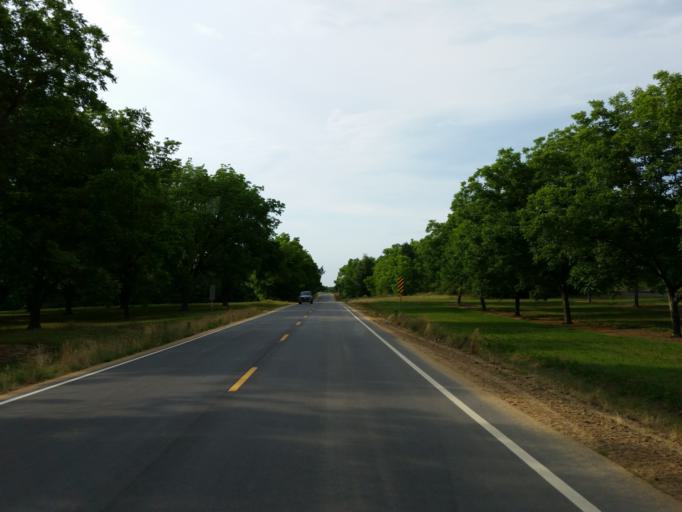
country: US
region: Georgia
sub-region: Turner County
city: Ashburn
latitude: 31.7995
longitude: -83.7108
